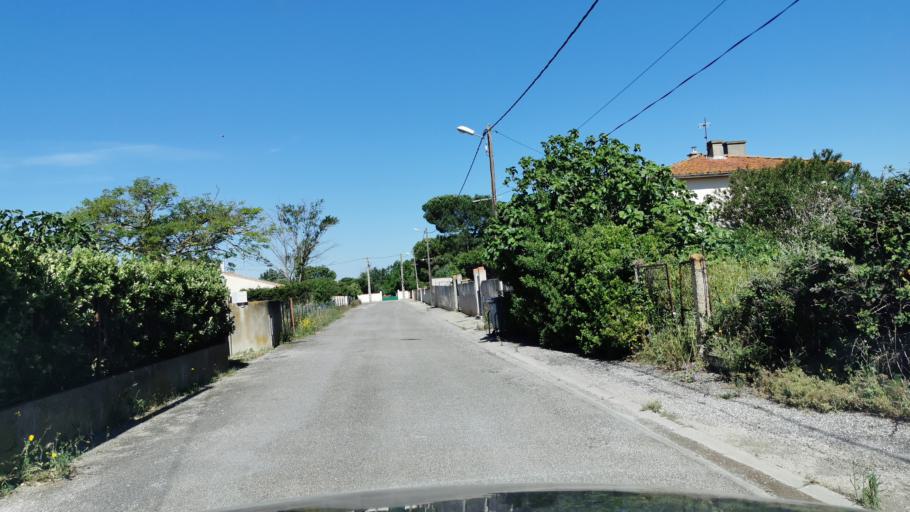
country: FR
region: Languedoc-Roussillon
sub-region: Departement de l'Aude
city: Canet
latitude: 43.2159
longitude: 2.8590
